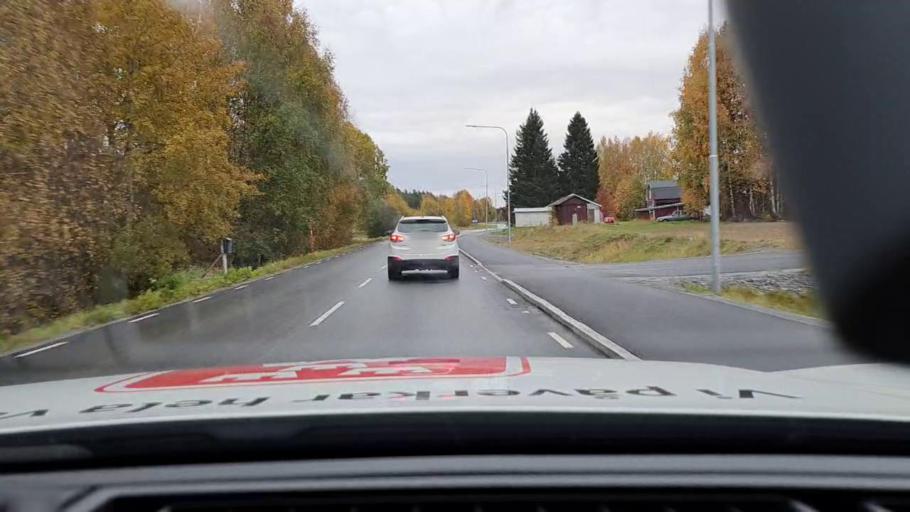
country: SE
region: Norrbotten
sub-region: Bodens Kommun
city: Saevast
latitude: 65.7728
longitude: 21.6990
